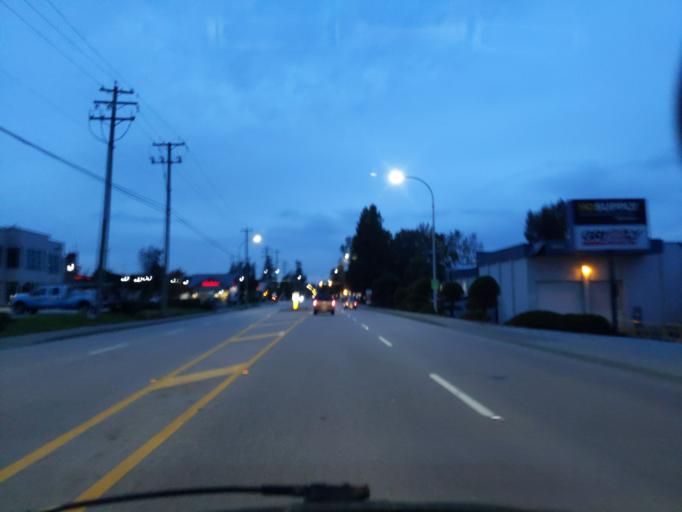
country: CA
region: British Columbia
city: Pitt Meadows
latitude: 49.1770
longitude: -122.6879
